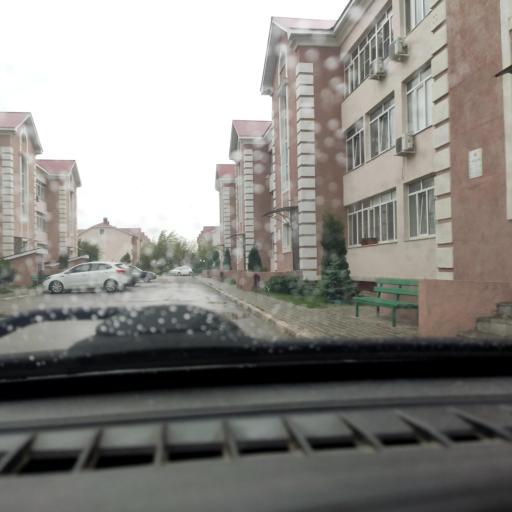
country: RU
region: Samara
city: Podstepki
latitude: 53.5295
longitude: 49.1776
